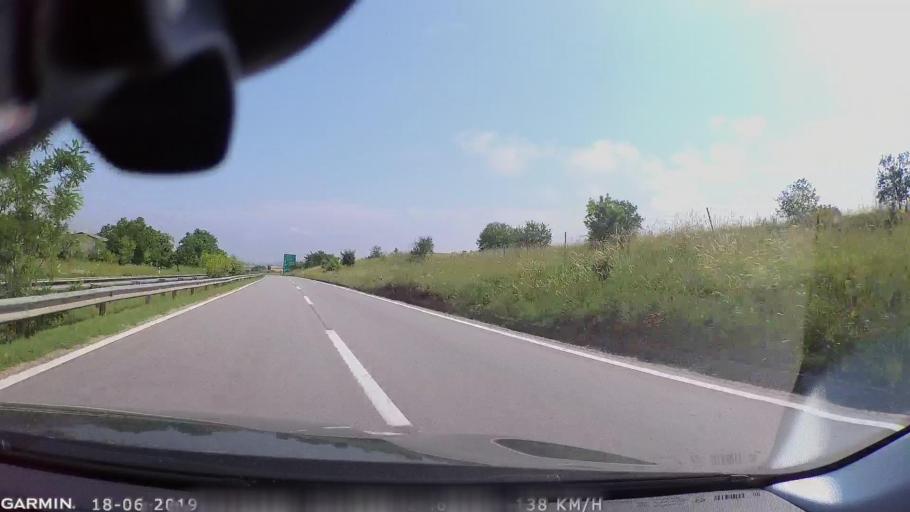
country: MK
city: Miladinovci
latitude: 41.9778
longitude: 21.6518
